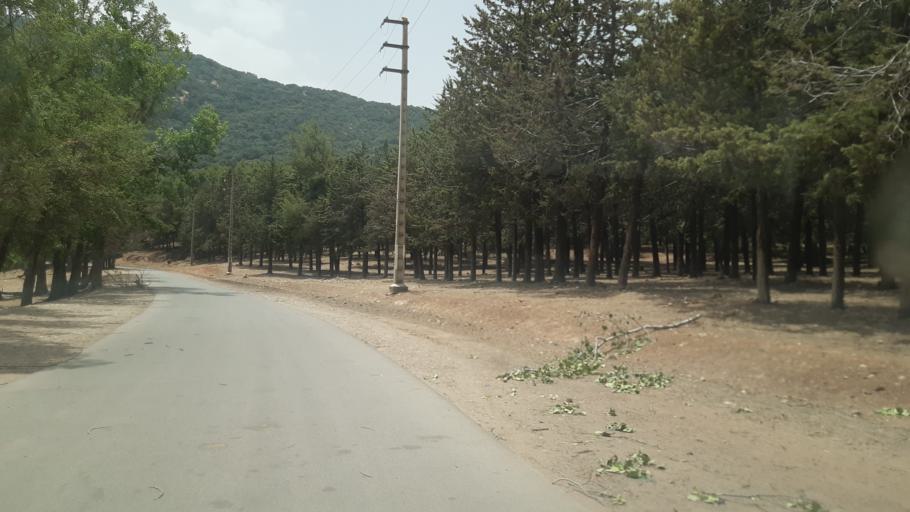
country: MA
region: Meknes-Tafilalet
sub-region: Ifrane
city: Ifrane
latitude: 33.6567
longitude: -5.0441
